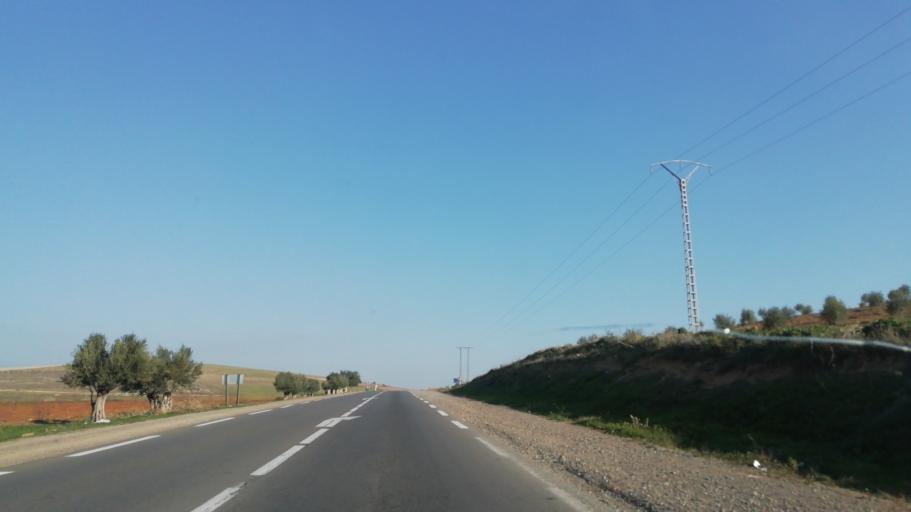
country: DZ
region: Ain Temouchent
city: Hammam Bou Hadjar
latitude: 35.1652
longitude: -0.8792
